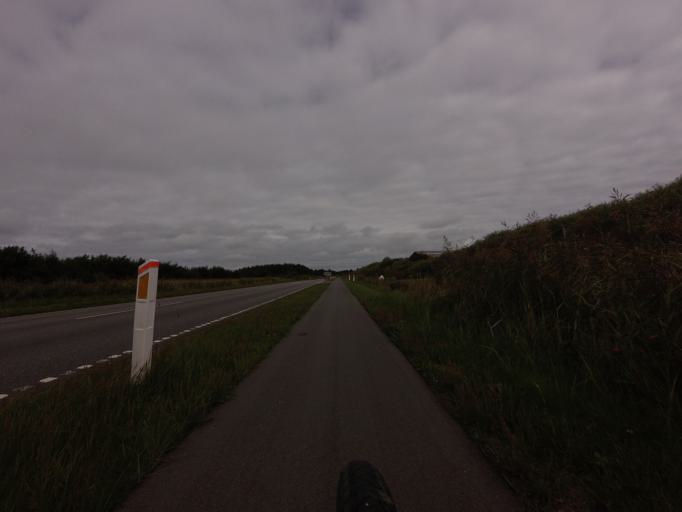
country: DK
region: North Denmark
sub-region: Hjorring Kommune
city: Hirtshals
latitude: 57.5695
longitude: 9.9425
